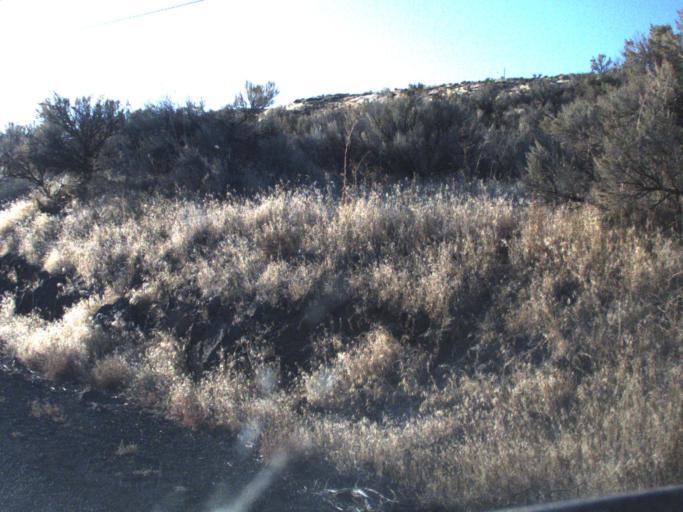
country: US
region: Washington
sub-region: Franklin County
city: Connell
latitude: 46.6461
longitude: -118.5450
